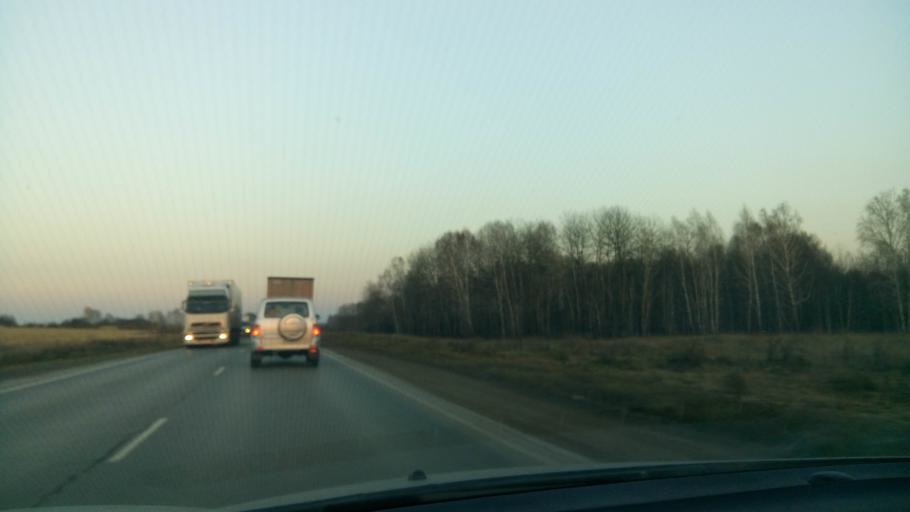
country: RU
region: Sverdlovsk
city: Pyshma
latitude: 56.8927
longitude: 63.0422
